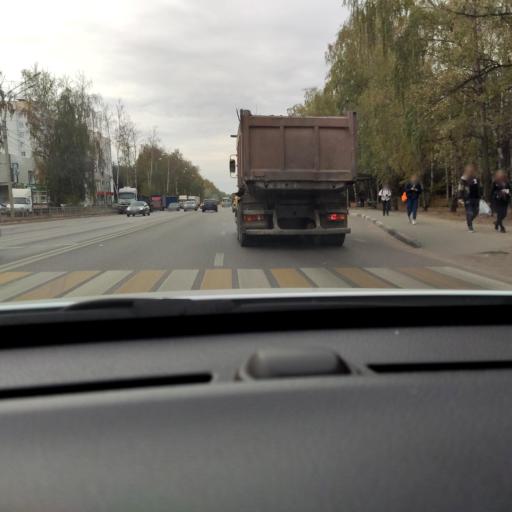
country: RU
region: Voronezj
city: Pridonskoy
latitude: 51.6872
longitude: 39.1098
